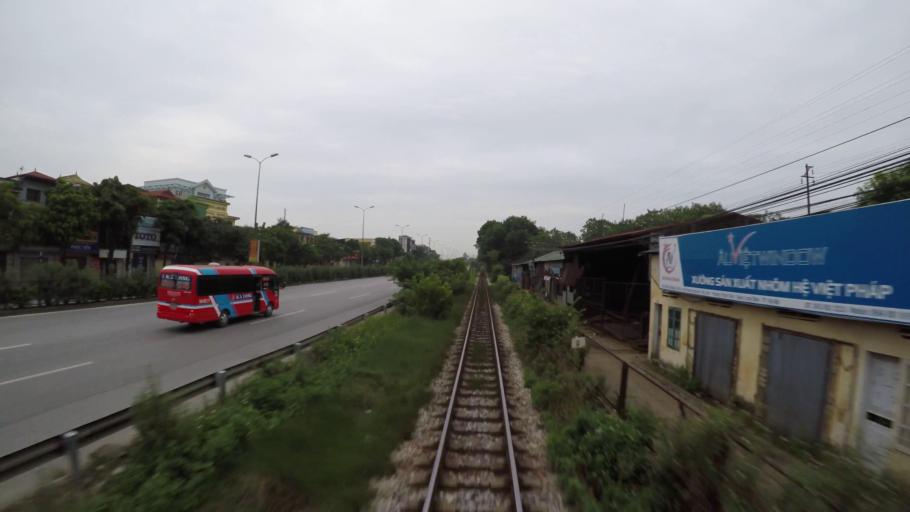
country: VN
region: Ha Noi
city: Trau Quy
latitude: 21.0031
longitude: 105.9628
